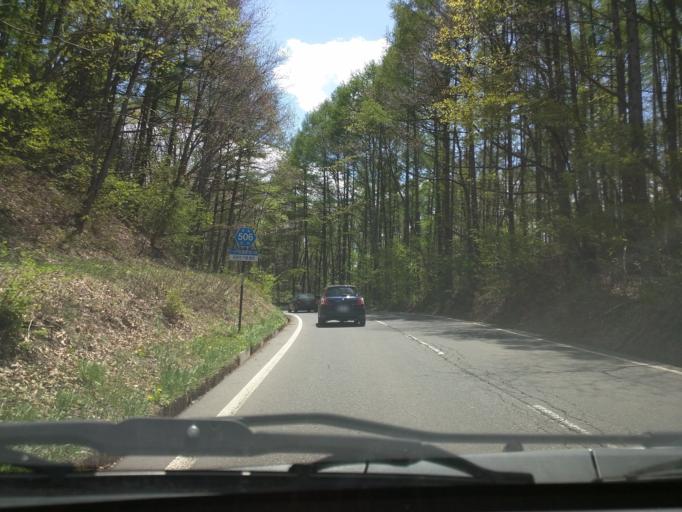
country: JP
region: Nagano
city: Nagano-shi
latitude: 36.7168
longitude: 138.1075
